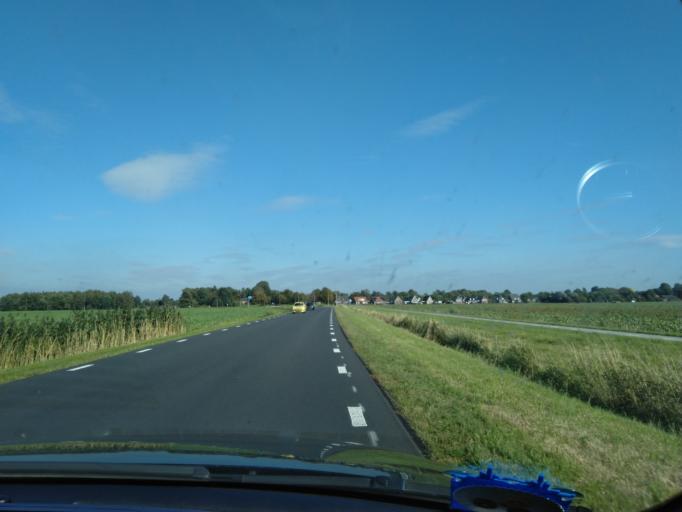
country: NL
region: Groningen
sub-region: Gemeente Hoogezand-Sappemeer
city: Sappemeer
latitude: 53.0826
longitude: 6.7829
